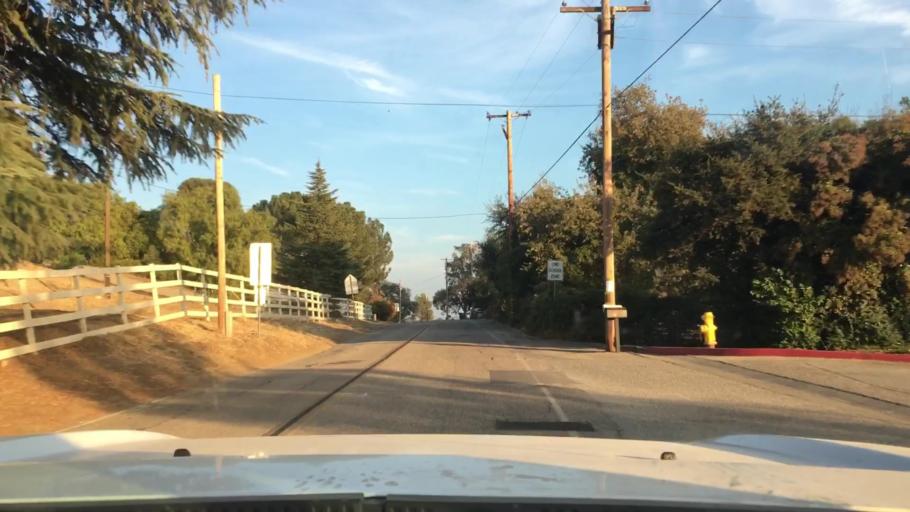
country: US
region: California
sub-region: San Luis Obispo County
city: Atascadero
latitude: 35.4590
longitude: -120.6678
